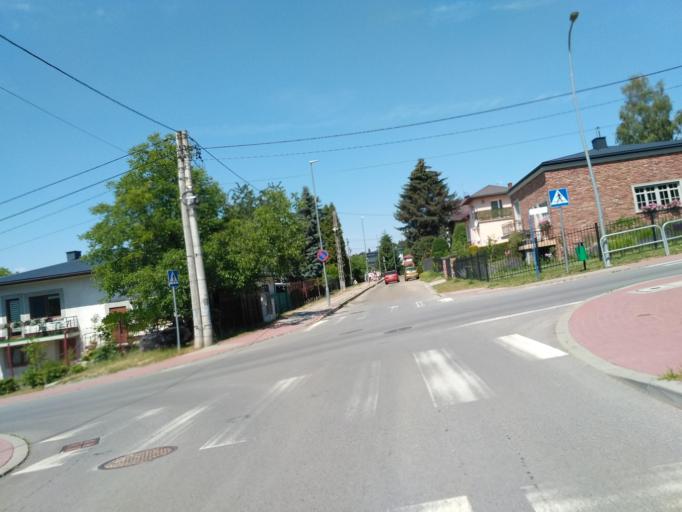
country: PL
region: Subcarpathian Voivodeship
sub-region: Krosno
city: Krosno
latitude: 49.6979
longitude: 21.7724
